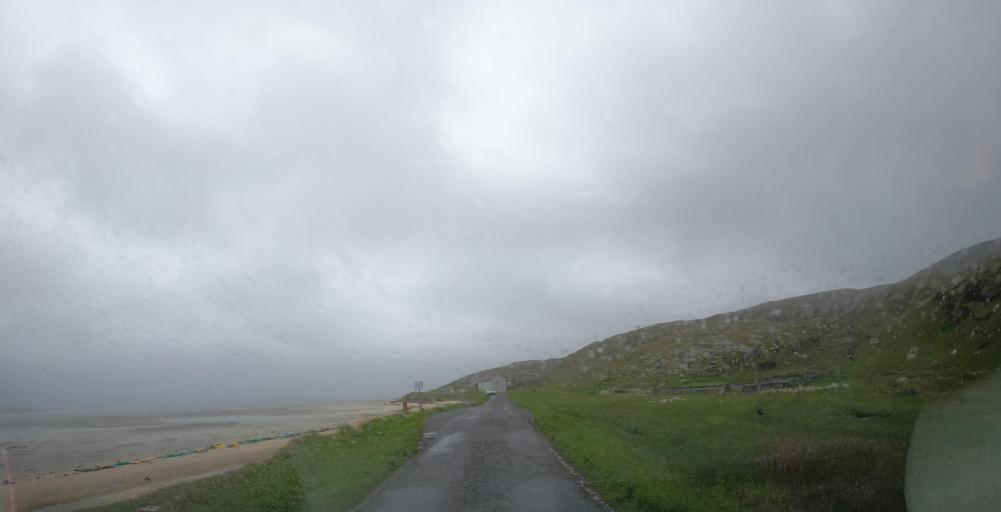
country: GB
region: Scotland
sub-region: Eilean Siar
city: Barra
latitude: 57.0196
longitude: -7.4458
